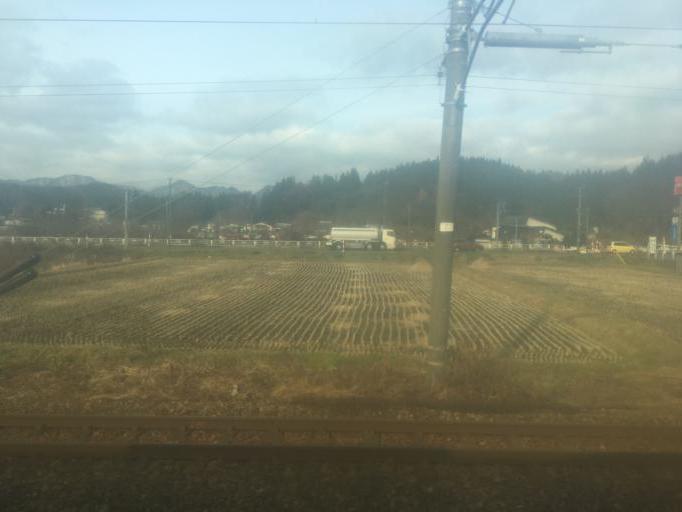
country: JP
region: Akita
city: Odate
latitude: 40.3408
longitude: 140.5952
